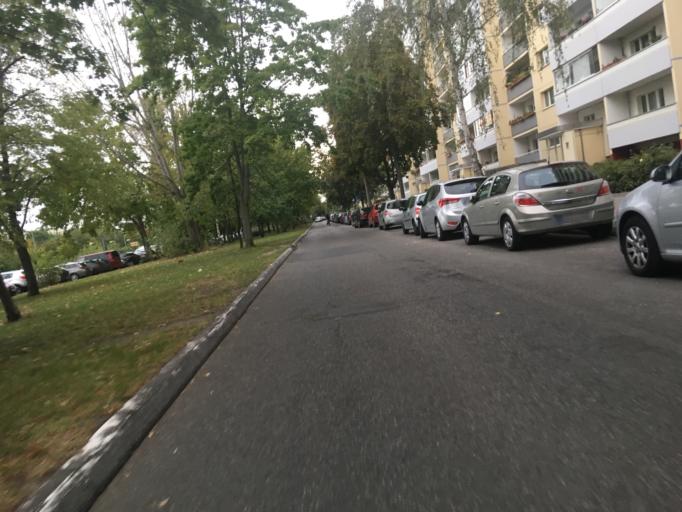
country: DE
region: Berlin
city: Fennpfuhl
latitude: 52.5347
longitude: 13.4828
